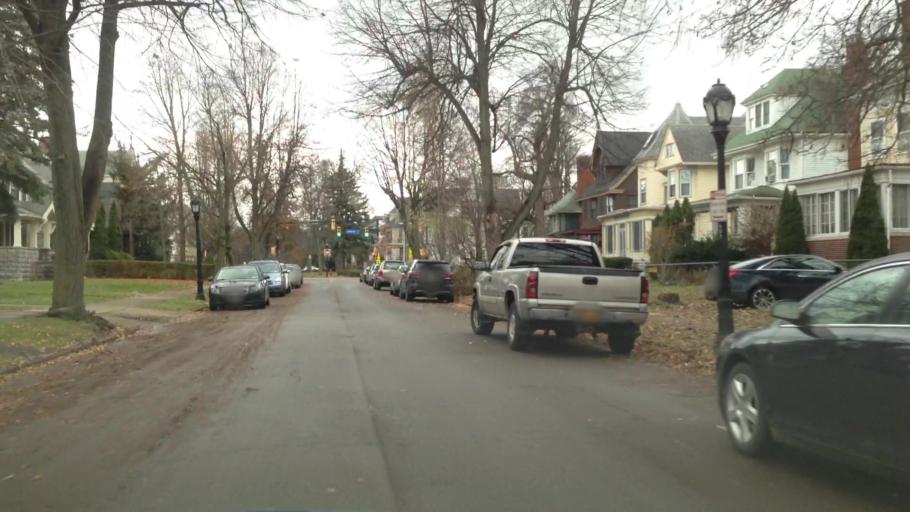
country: US
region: New York
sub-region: Erie County
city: Kenmore
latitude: 42.9414
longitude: -78.8493
